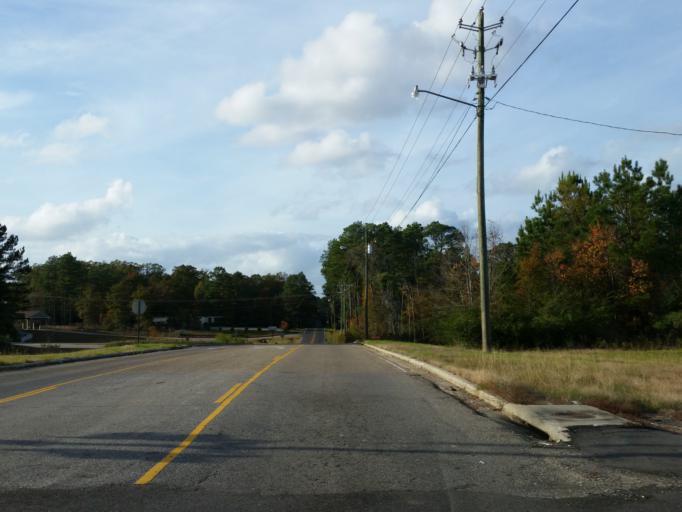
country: US
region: Mississippi
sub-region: Forrest County
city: Hattiesburg
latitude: 31.2909
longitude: -89.3258
